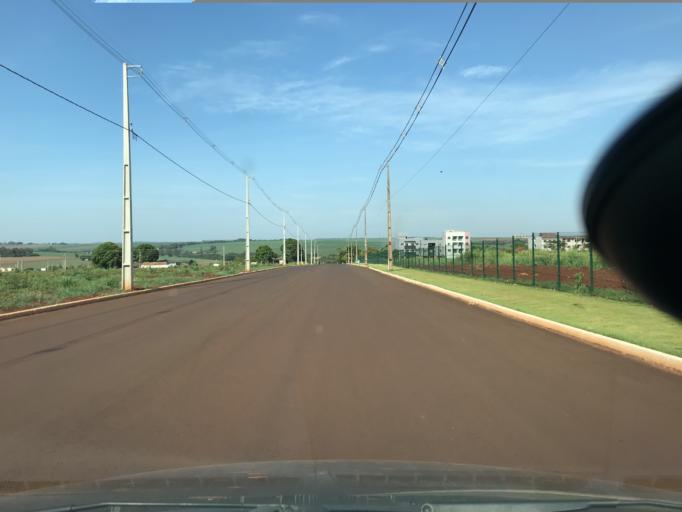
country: BR
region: Parana
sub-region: Palotina
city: Palotina
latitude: -24.2973
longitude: -53.8400
